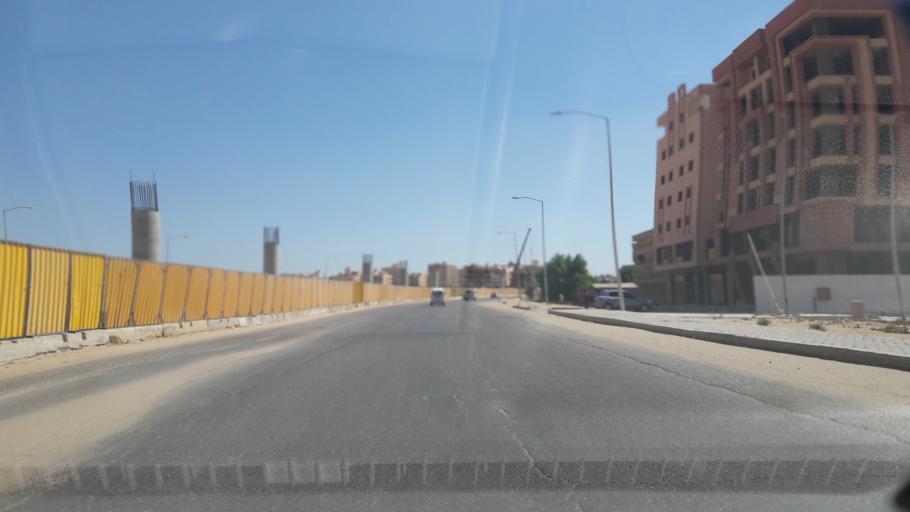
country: EG
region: Al Jizah
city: Madinat Sittah Uktubar
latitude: 29.9667
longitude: 30.9308
